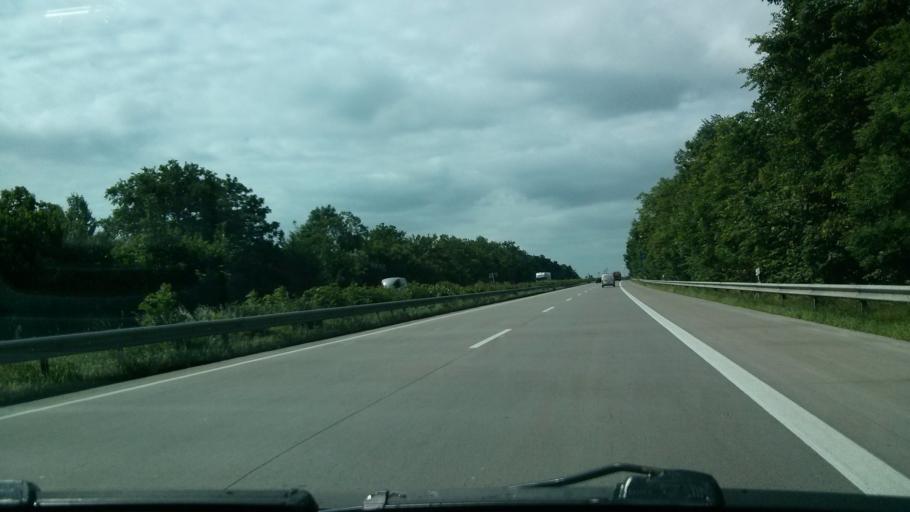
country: DE
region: Lower Saxony
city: Loxstedt
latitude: 53.4710
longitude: 8.6094
